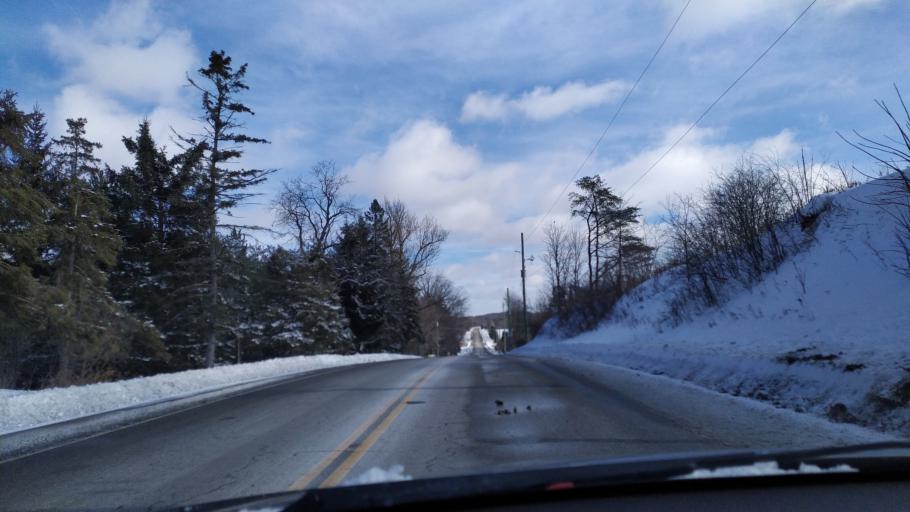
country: CA
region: Ontario
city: Waterloo
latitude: 43.4748
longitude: -80.6940
